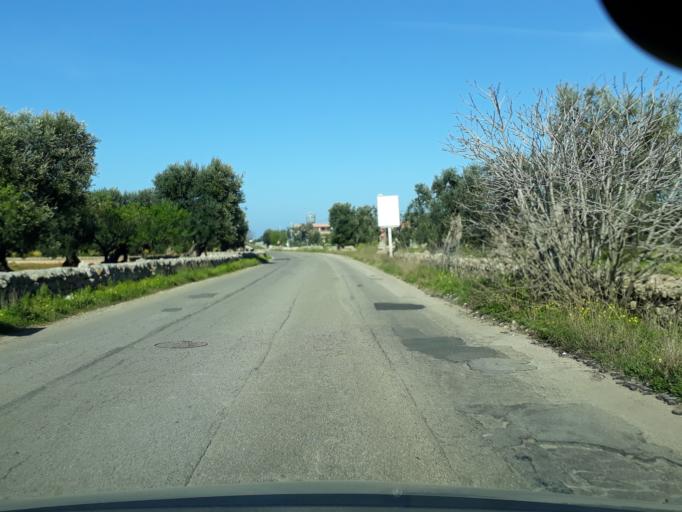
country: IT
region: Apulia
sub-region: Provincia di Bari
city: Monopoli
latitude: 40.9317
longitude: 17.2891
